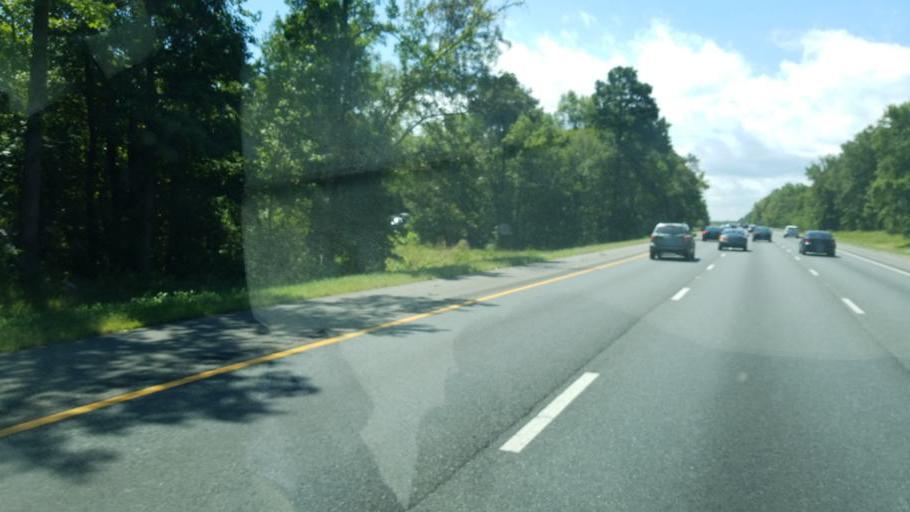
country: US
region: Virginia
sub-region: Spotsylvania County
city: Spotsylvania Courthouse
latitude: 38.1059
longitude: -77.5183
